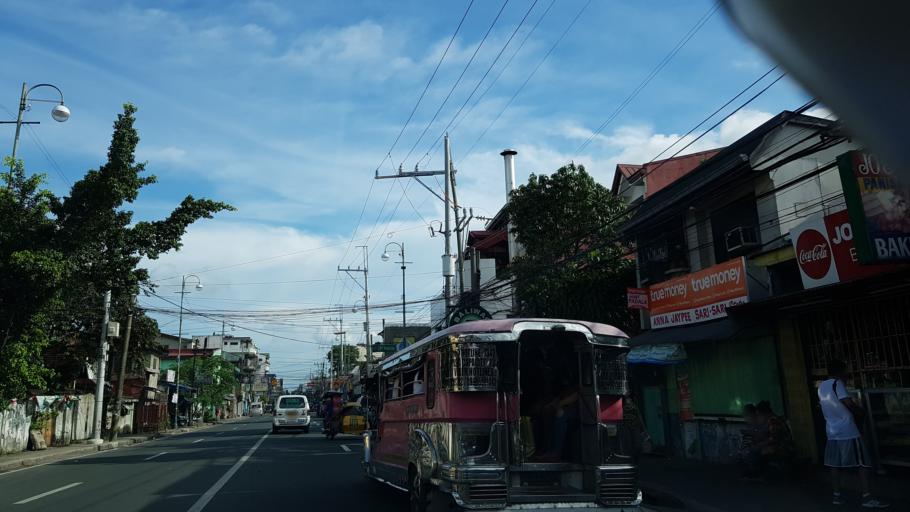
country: PH
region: Calabarzon
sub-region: Province of Rizal
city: Pateros
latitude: 14.5508
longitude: 121.0634
